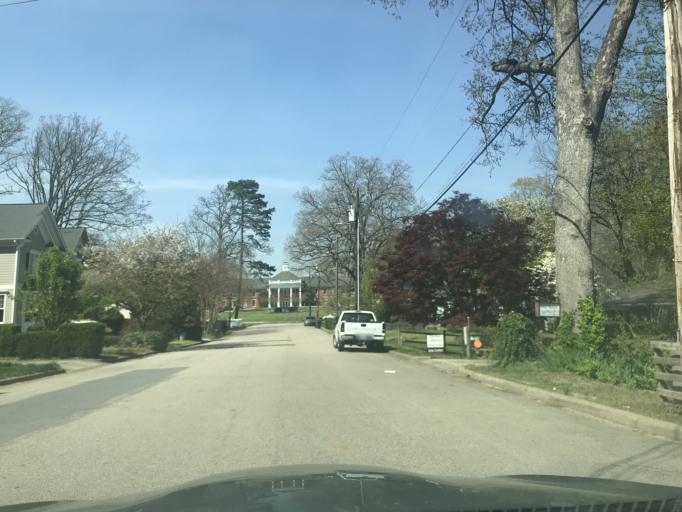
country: US
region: North Carolina
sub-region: Wake County
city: Raleigh
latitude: 35.8062
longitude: -78.6349
